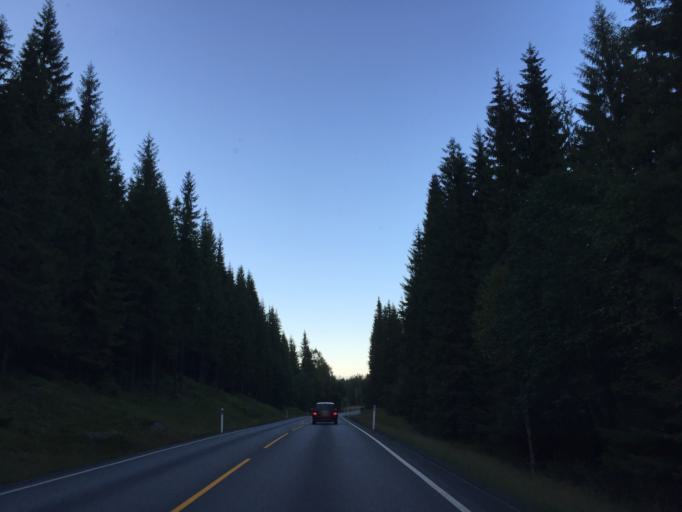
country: NO
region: Hedmark
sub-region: Nord-Odal
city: Sand
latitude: 60.5116
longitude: 11.5082
